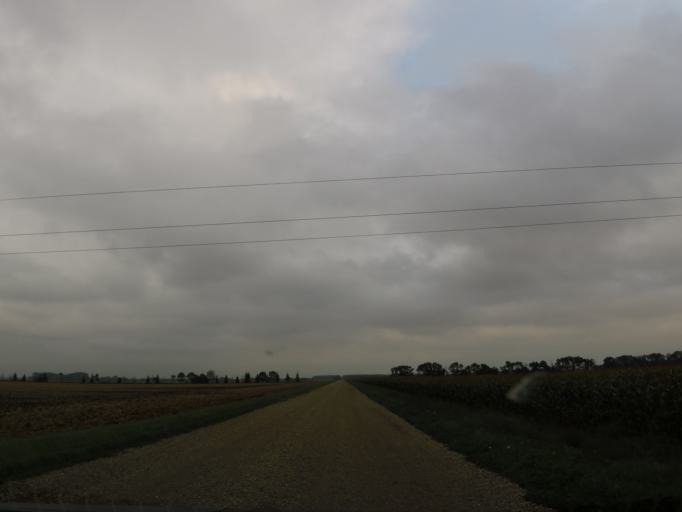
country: US
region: North Dakota
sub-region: Walsh County
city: Grafton
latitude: 48.4704
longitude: -97.1853
